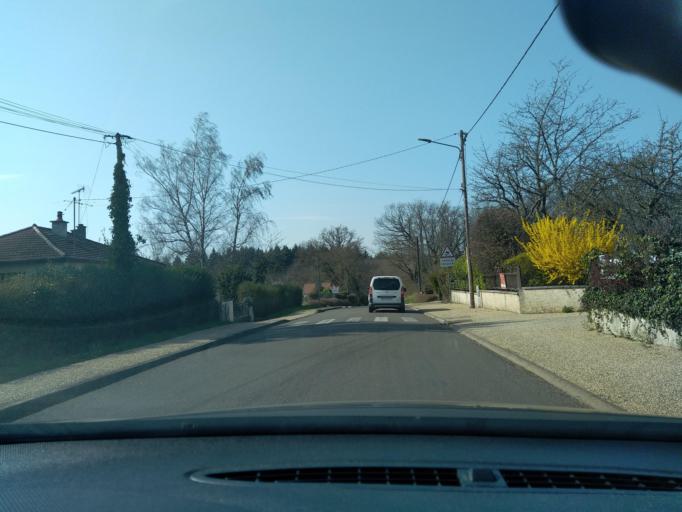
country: FR
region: Franche-Comte
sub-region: Departement du Jura
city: Dole
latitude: 47.0438
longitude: 5.5220
